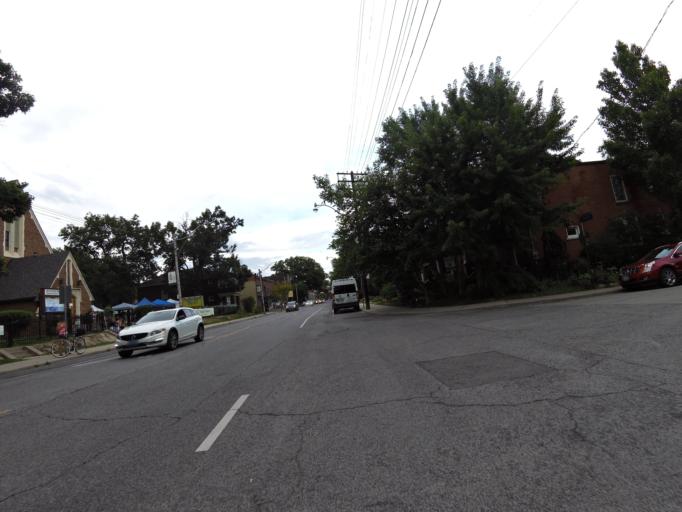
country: CA
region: Ontario
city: Toronto
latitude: 43.6589
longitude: -79.4851
